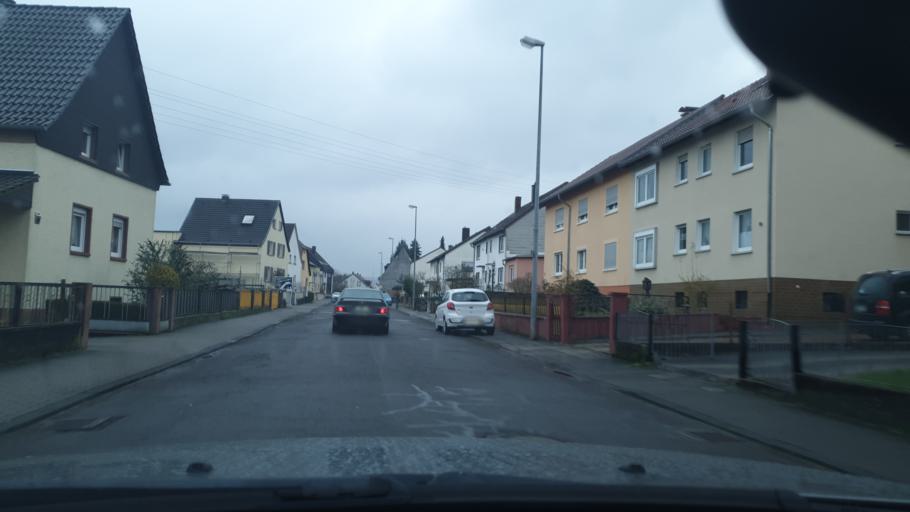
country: DE
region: Rheinland-Pfalz
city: Zweibrucken
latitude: 49.2488
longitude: 7.3406
